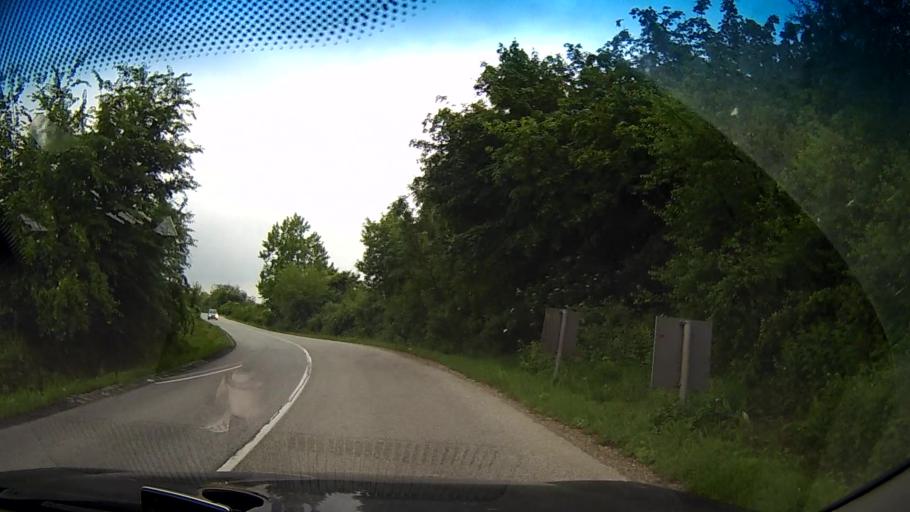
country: HU
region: Pest
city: Perbal
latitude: 47.6046
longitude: 18.7683
